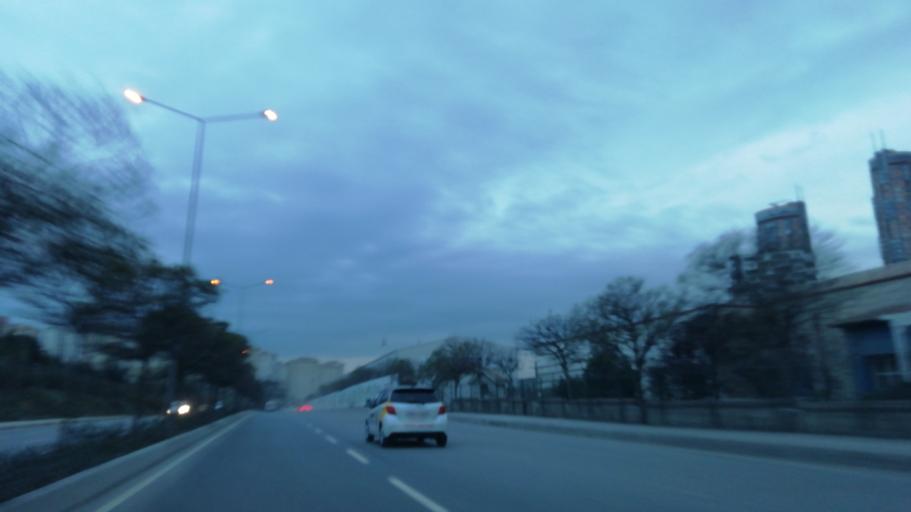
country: TR
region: Istanbul
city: Mahmutbey
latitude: 41.0442
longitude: 28.7738
